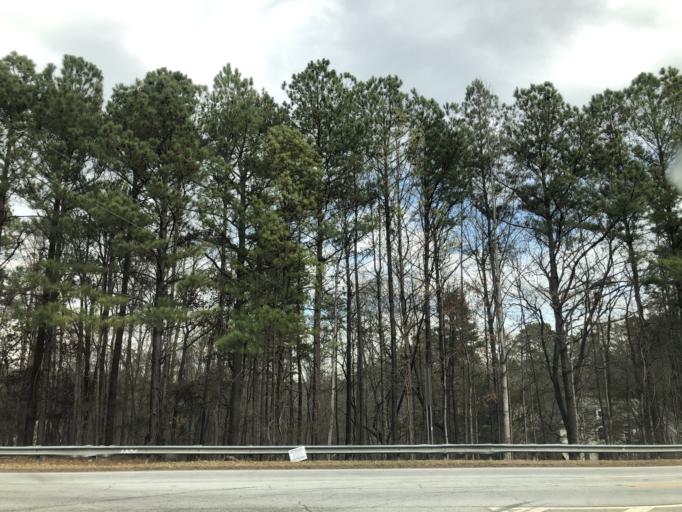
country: US
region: Georgia
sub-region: DeKalb County
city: Pine Mountain
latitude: 33.6654
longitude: -84.1974
